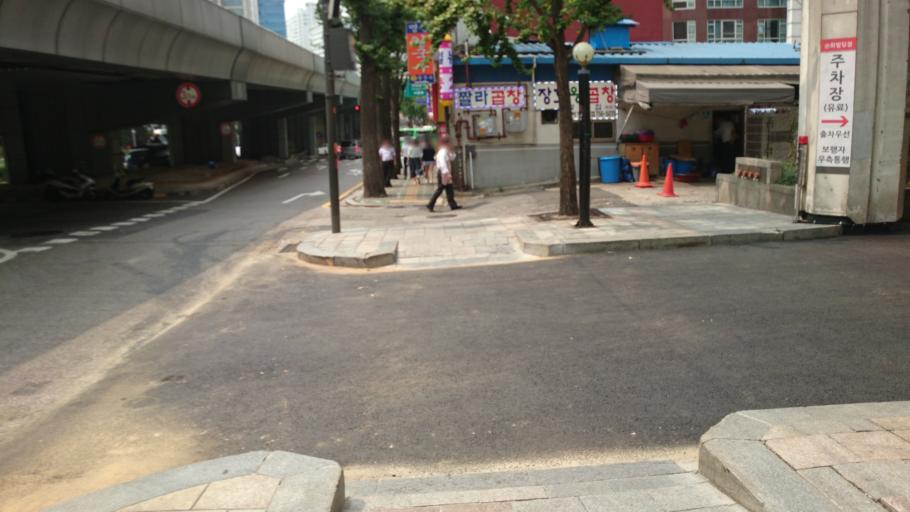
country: KR
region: Seoul
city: Seoul
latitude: 37.5616
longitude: 126.9707
